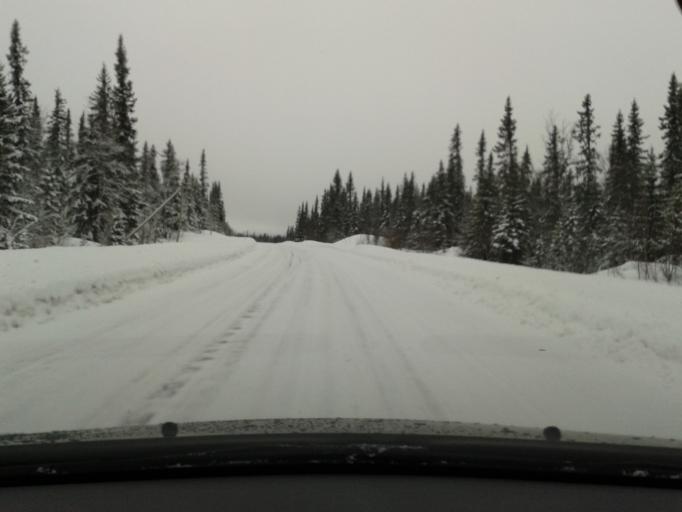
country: SE
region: Vaesterbotten
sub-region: Vilhelmina Kommun
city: Sjoberg
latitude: 65.1589
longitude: 15.8665
